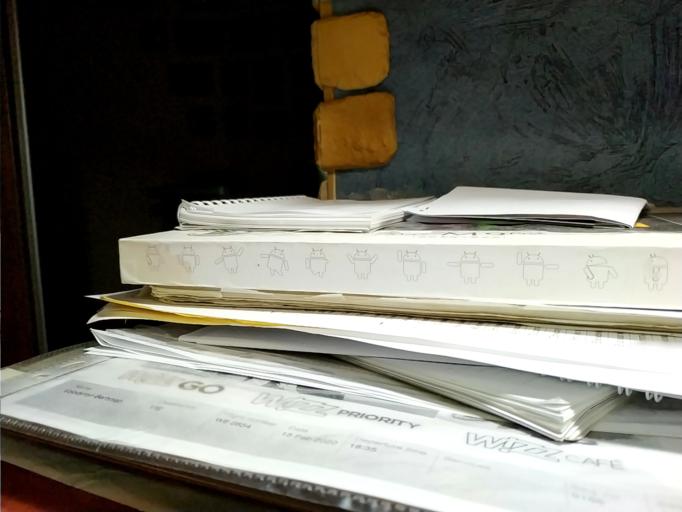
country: RU
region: Arkhangelskaya
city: Onega
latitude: 63.5316
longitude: 38.1271
